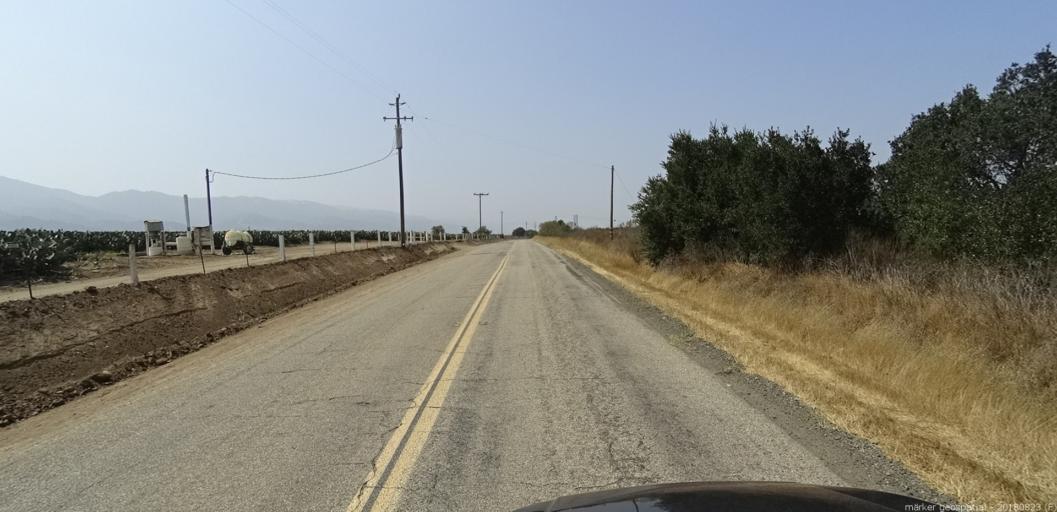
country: US
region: California
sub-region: Monterey County
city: Gonzales
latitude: 36.4508
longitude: -121.4381
